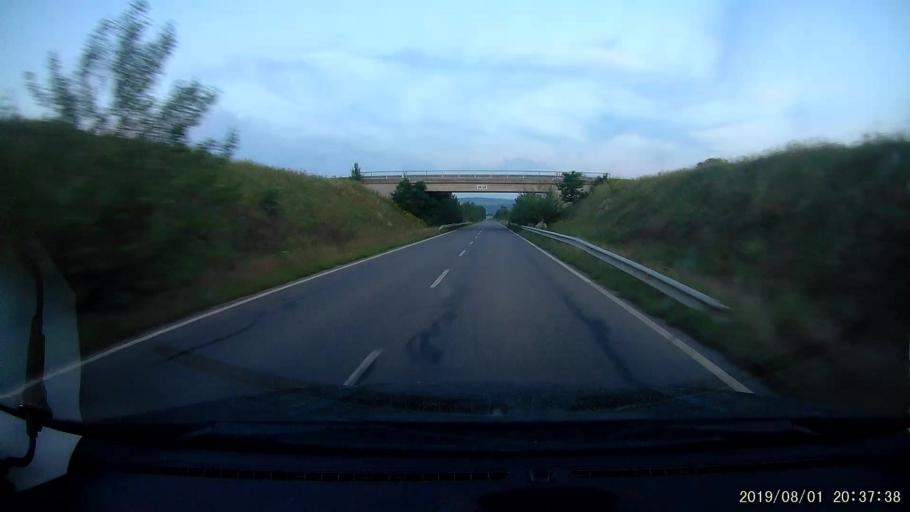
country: BG
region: Yambol
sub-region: Obshtina Elkhovo
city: Elkhovo
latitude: 42.0439
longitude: 26.5950
